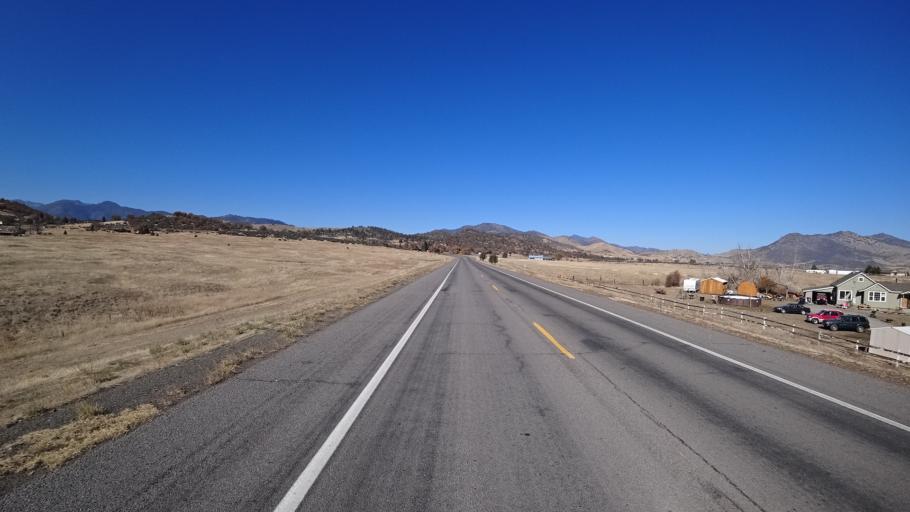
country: US
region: California
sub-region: Siskiyou County
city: Yreka
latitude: 41.7378
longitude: -122.5959
